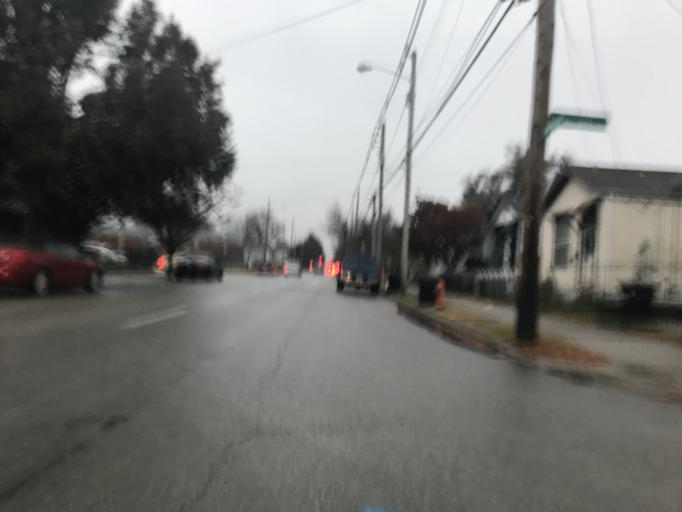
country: US
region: Kentucky
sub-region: Jefferson County
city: Louisville
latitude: 38.2428
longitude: -85.7399
